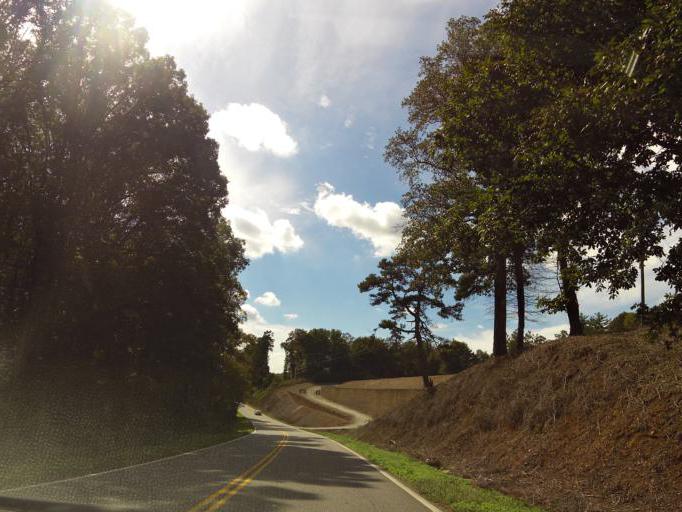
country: US
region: Georgia
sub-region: Pickens County
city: Nelson
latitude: 34.4466
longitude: -84.2739
